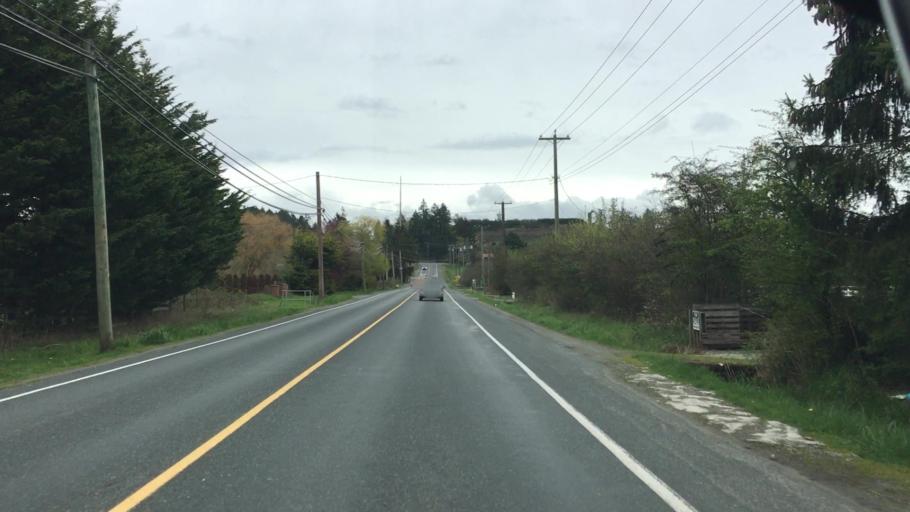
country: CA
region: British Columbia
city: North Saanich
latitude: 48.5651
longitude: -123.4353
